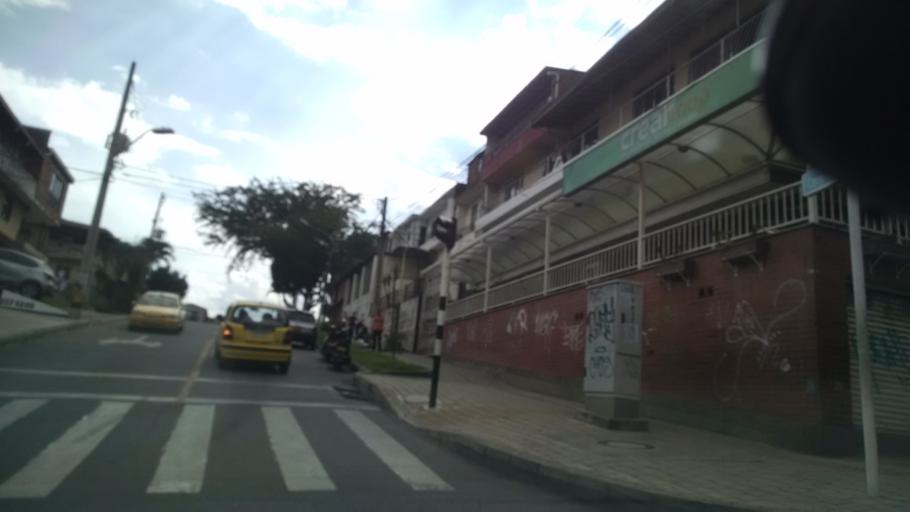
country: CO
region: Antioquia
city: Bello
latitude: 6.3015
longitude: -75.5722
